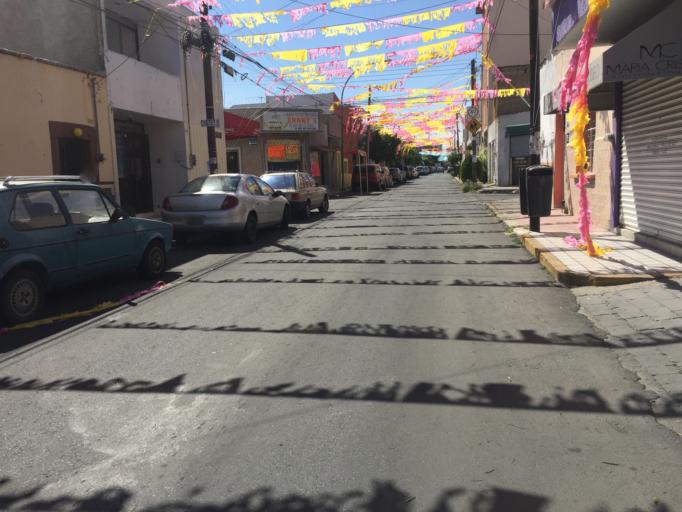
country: MX
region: Jalisco
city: Guadalajara
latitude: 20.6869
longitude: -103.3649
